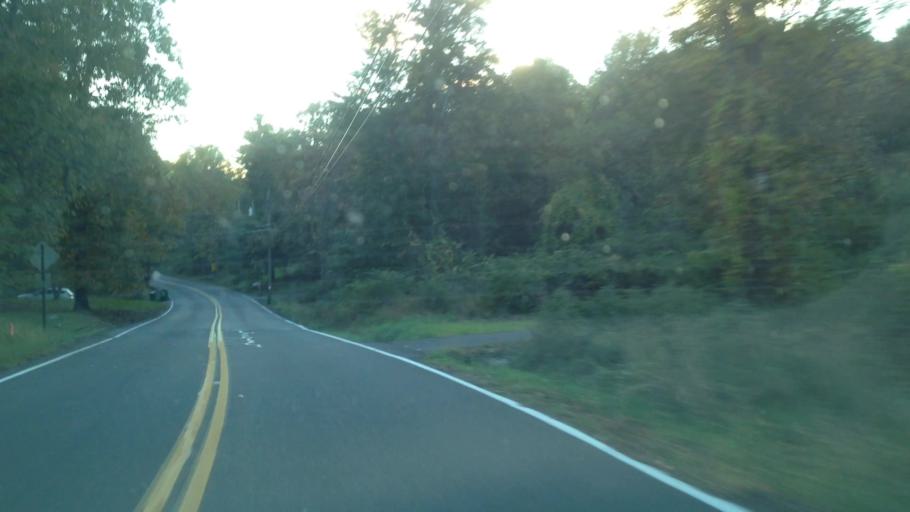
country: US
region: New York
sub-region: Dutchess County
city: Hyde Park
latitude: 41.8278
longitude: -73.9896
